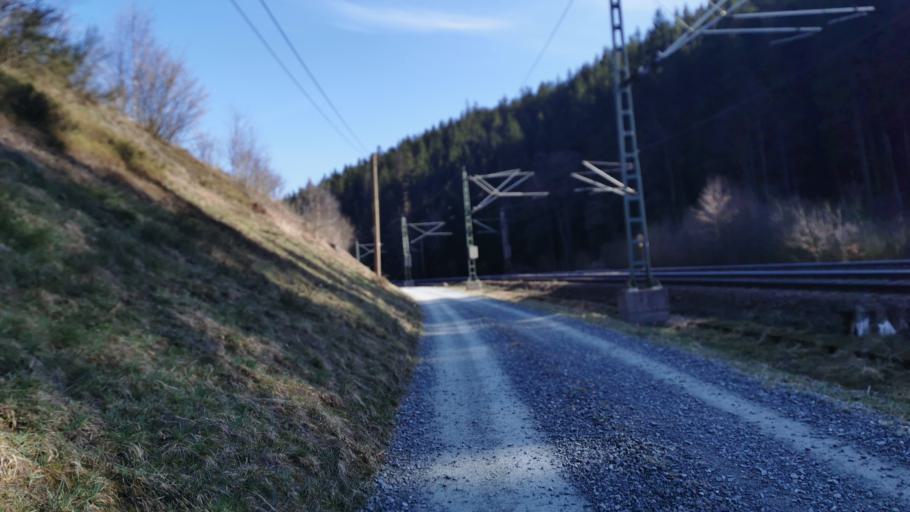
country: DE
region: Bavaria
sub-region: Upper Franconia
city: Teuschnitz
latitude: 50.4071
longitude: 11.3612
